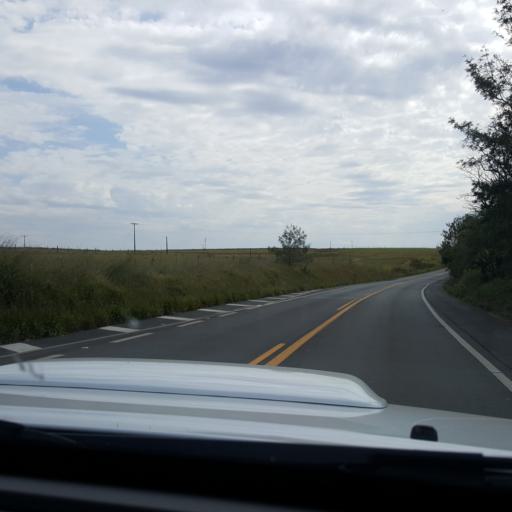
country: BR
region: Sao Paulo
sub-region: Itaporanga
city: Itaporanga
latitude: -23.7710
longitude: -49.4417
